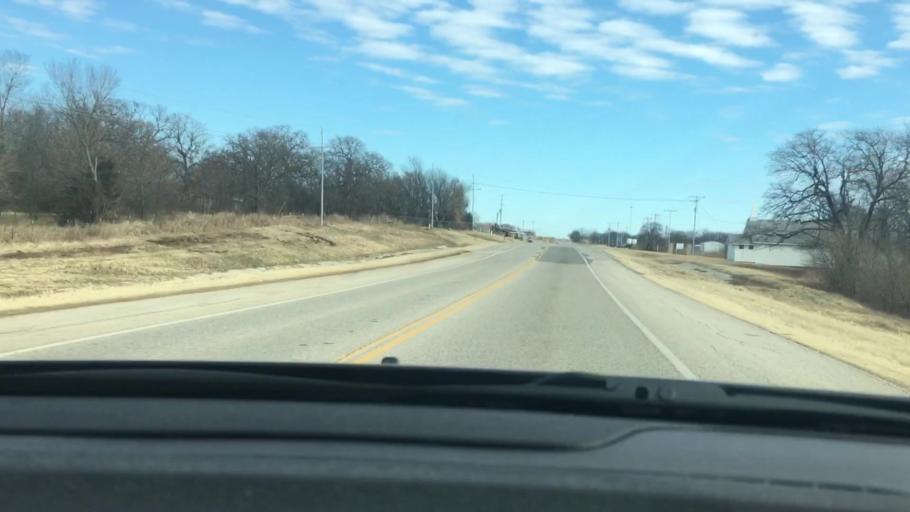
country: US
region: Oklahoma
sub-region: Garvin County
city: Stratford
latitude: 34.7968
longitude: -96.8655
